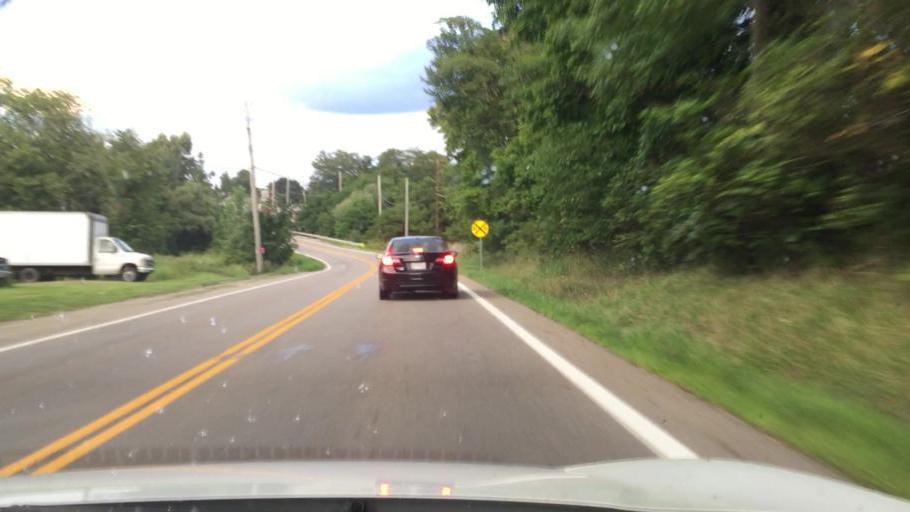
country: US
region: Ohio
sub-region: Champaign County
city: Mechanicsburg
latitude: 40.0680
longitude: -83.5625
